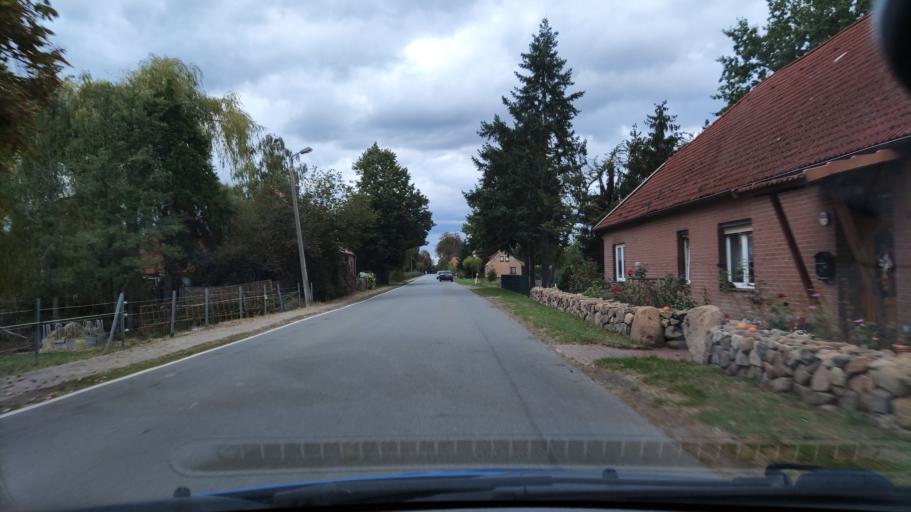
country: DE
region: Lower Saxony
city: Neu Darchau
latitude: 53.3121
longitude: 10.9587
